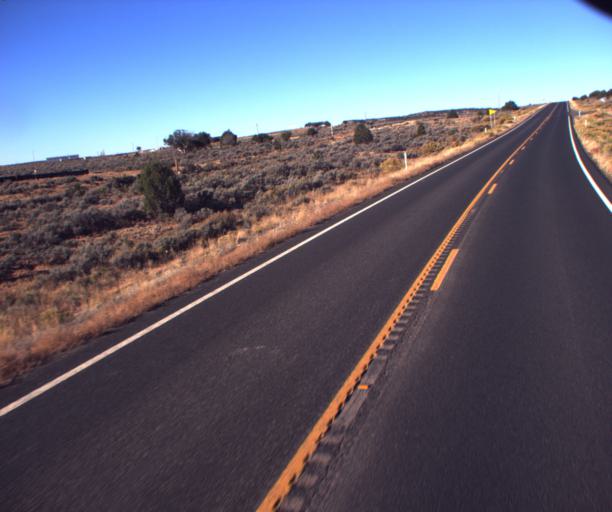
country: US
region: Arizona
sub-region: Apache County
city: Ganado
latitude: 35.7606
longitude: -109.7574
